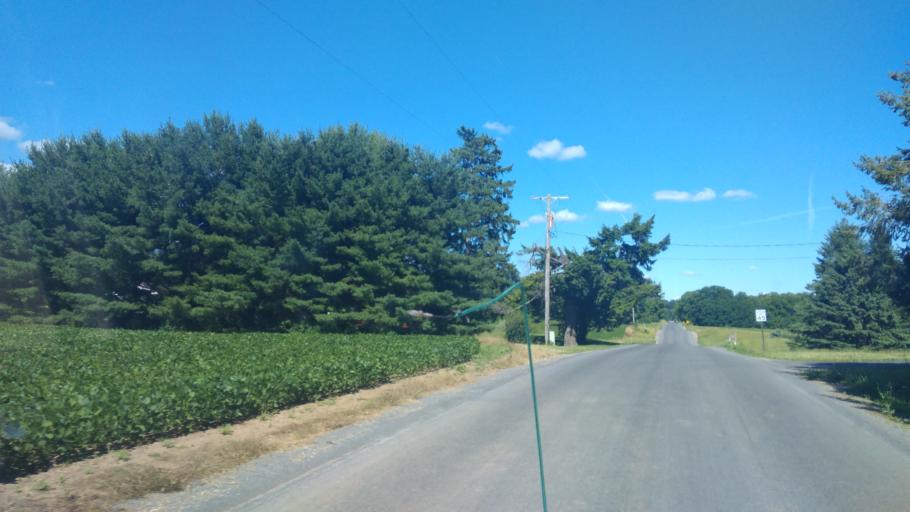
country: US
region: New York
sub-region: Wayne County
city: Clyde
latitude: 43.0263
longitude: -76.8900
